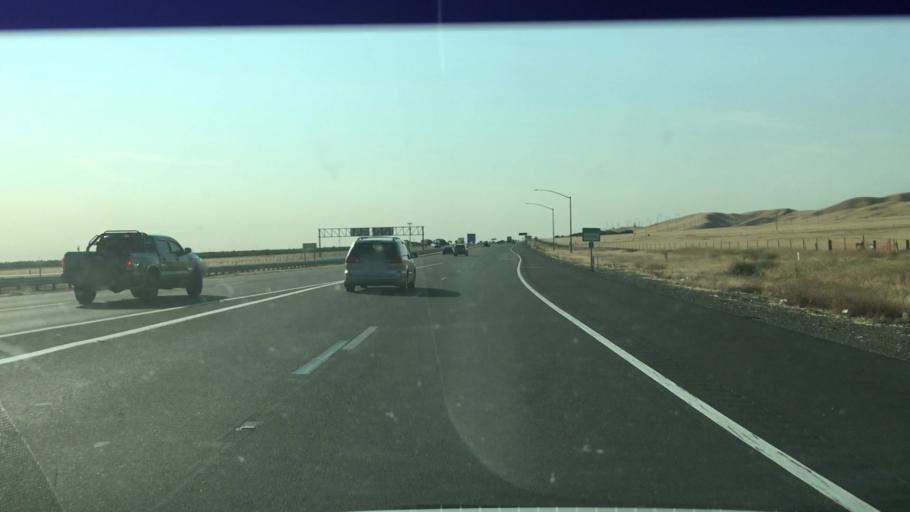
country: US
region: California
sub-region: San Joaquin County
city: Tracy
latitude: 37.5912
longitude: -121.3344
